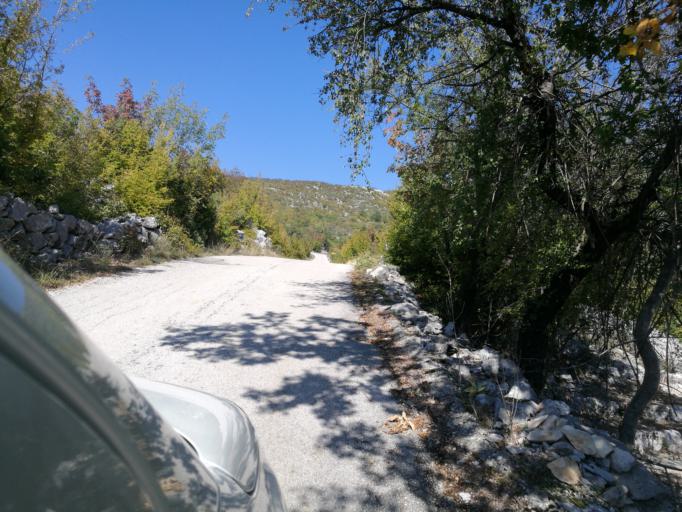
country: HR
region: Splitsko-Dalmatinska
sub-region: Grad Omis
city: Omis
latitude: 43.5153
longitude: 16.7278
